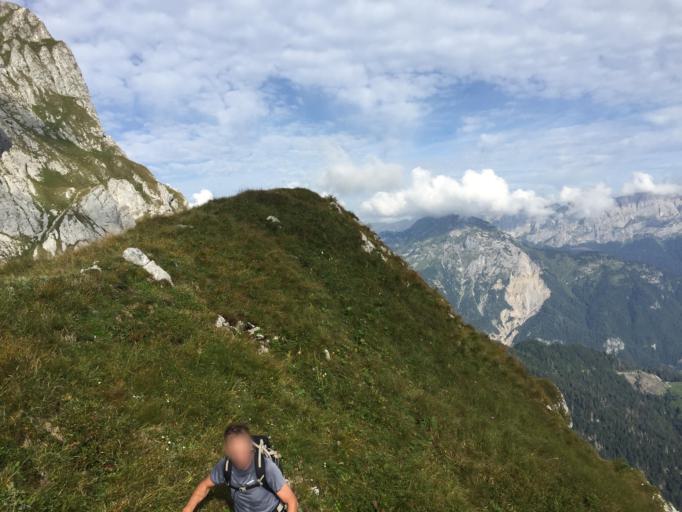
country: IT
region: Friuli Venezia Giulia
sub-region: Provincia di Udine
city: Pieria-Prato Carnico
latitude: 46.5495
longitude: 12.7883
